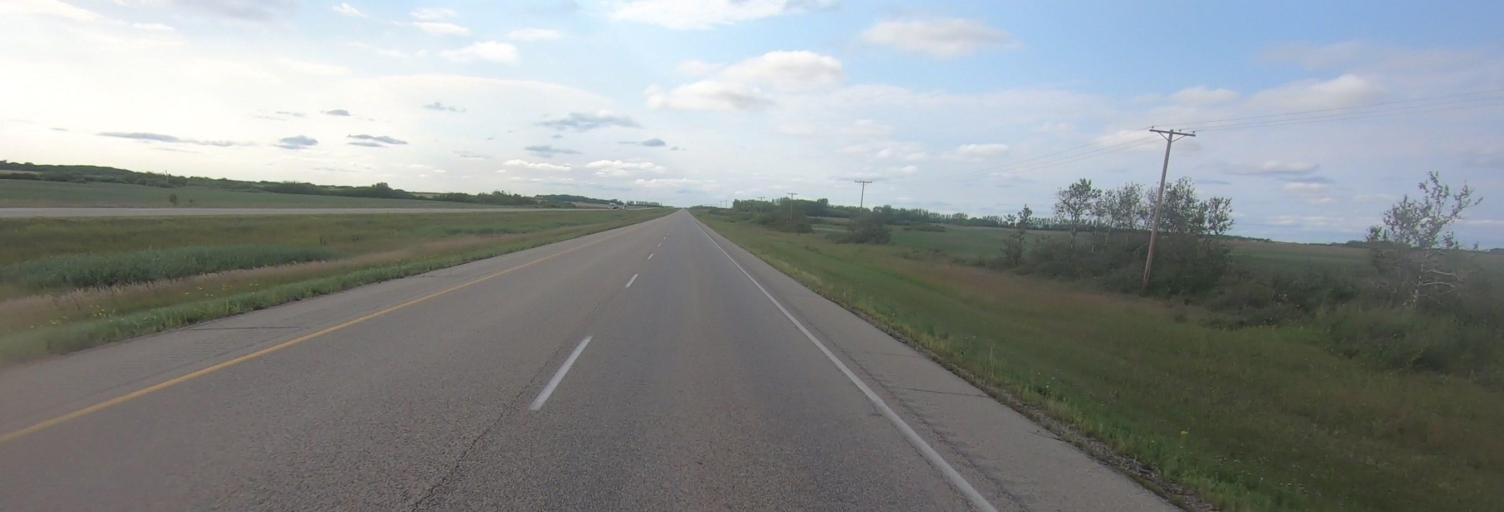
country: CA
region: Saskatchewan
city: Moosomin
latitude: 50.2218
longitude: -101.8295
